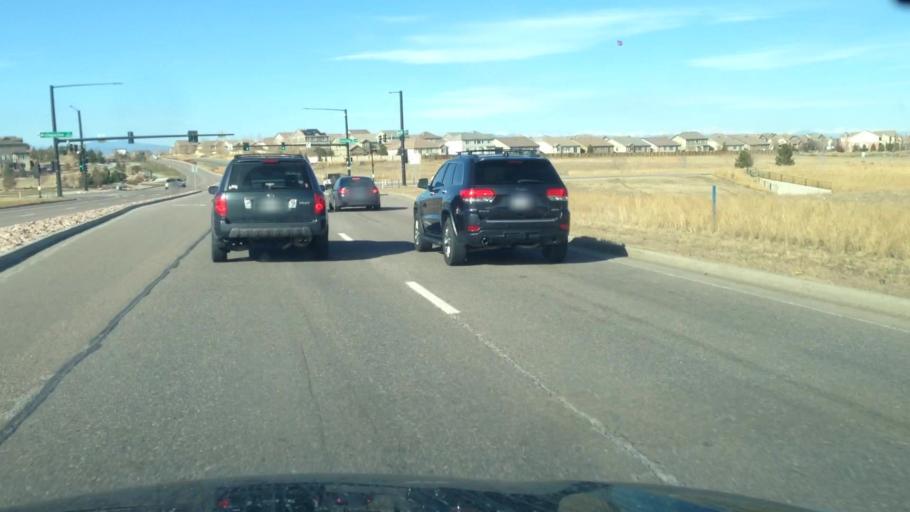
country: US
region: Colorado
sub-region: Douglas County
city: Stonegate
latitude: 39.5183
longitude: -104.8207
